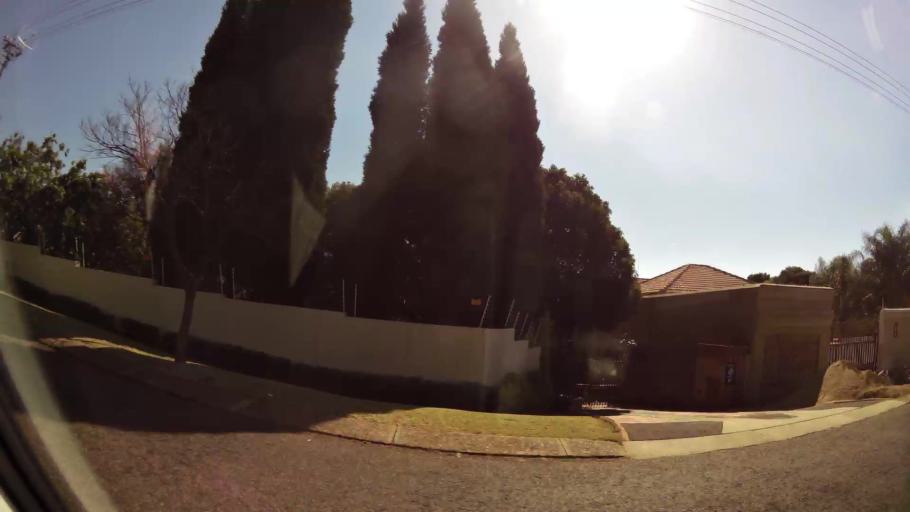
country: ZA
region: Gauteng
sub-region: City of Tshwane Metropolitan Municipality
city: Pretoria
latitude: -25.7971
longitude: 28.2420
